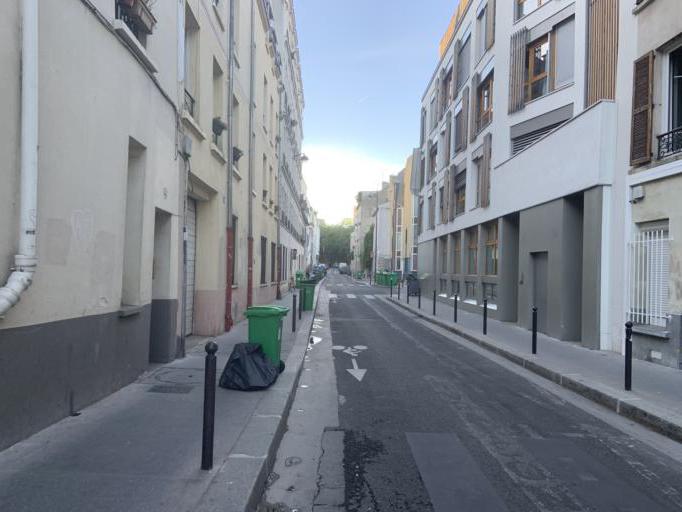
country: FR
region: Ile-de-France
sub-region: Departement de Seine-Saint-Denis
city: Bagnolet
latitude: 48.8535
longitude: 2.4066
